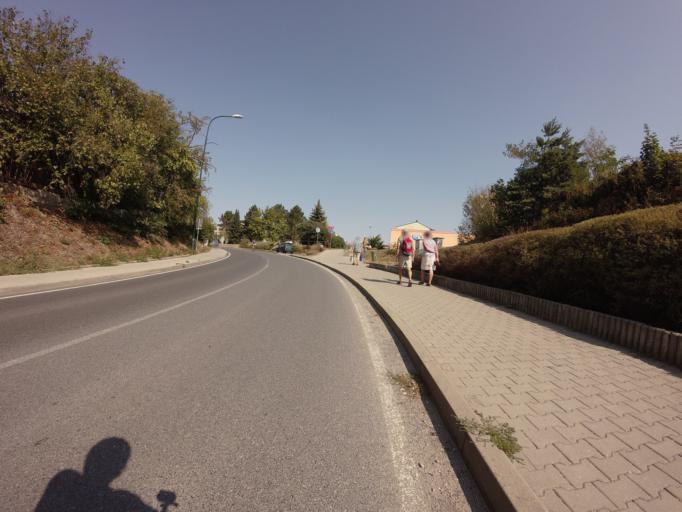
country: CZ
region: Central Bohemia
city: Tynec nad Sazavou
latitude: 49.8340
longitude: 14.5897
